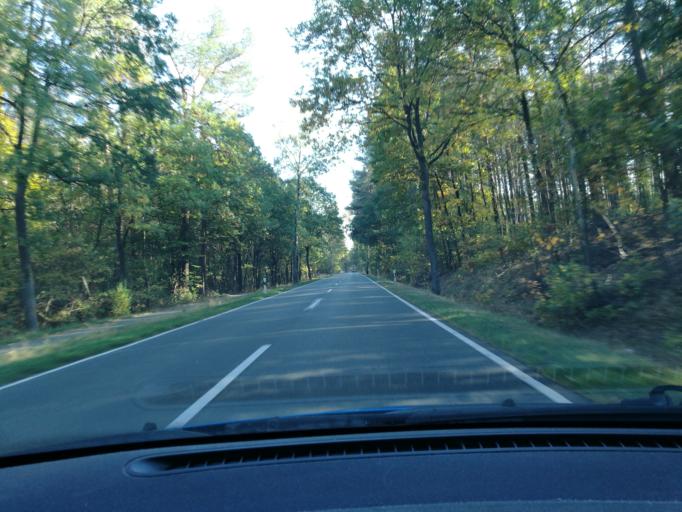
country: DE
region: Lower Saxony
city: Karwitz
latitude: 53.1233
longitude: 10.9822
